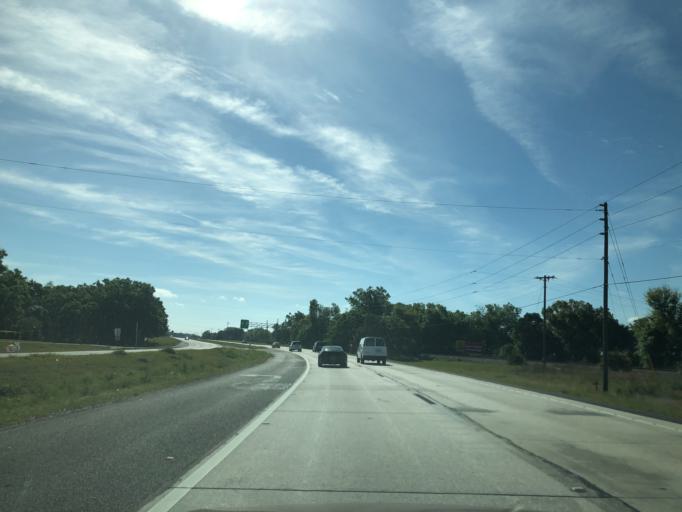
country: US
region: Florida
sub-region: Orange County
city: Zellwood
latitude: 28.7008
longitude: -81.5760
